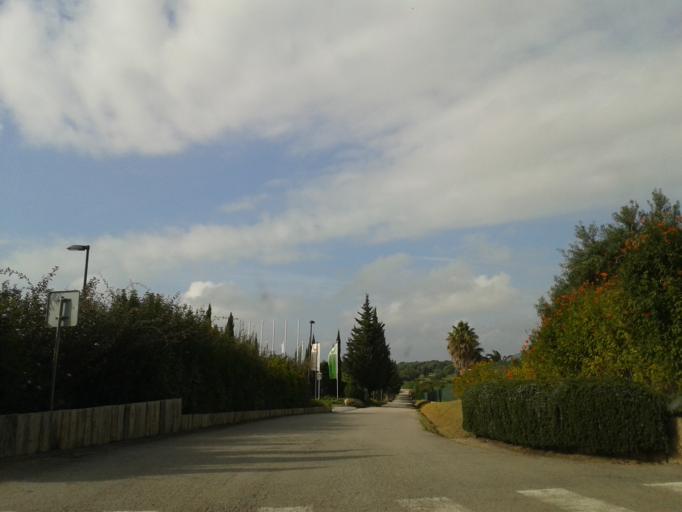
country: PT
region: Faro
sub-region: Tavira
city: Tavira
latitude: 37.1573
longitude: -7.5664
